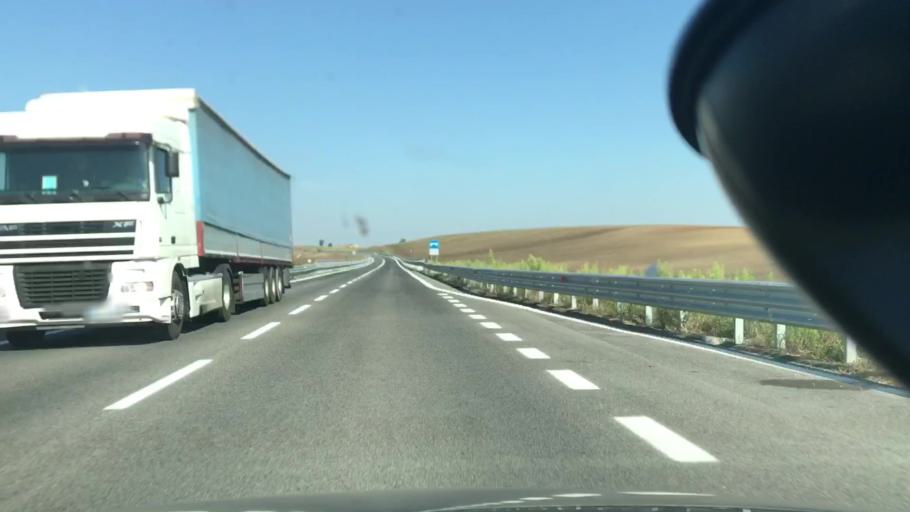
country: IT
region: Basilicate
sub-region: Provincia di Potenza
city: Palazzo San Gervasio
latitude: 40.9609
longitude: 16.0130
